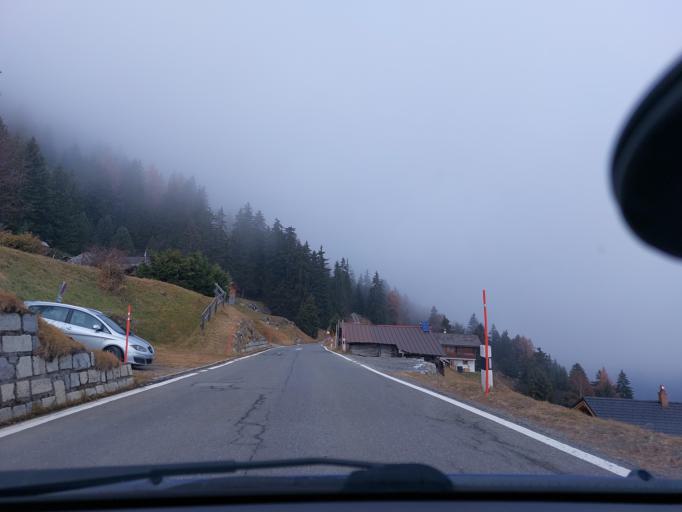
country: CH
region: Valais
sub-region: Conthey District
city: Basse-Nendaz
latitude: 46.1549
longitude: 7.3148
